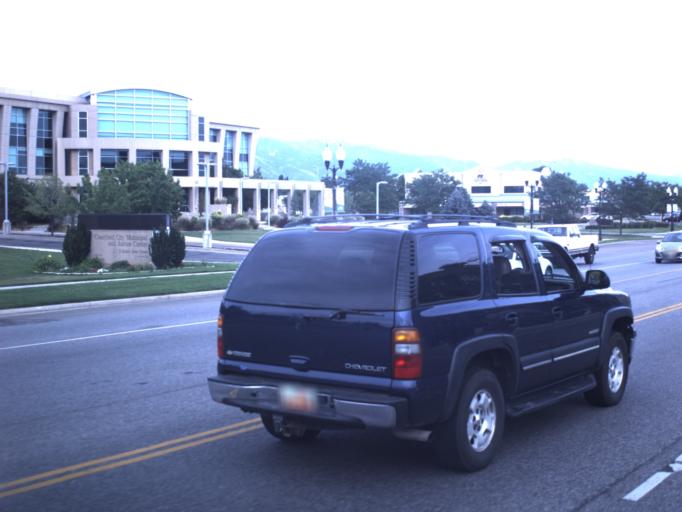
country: US
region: Utah
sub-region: Davis County
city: Clearfield
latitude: 41.1133
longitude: -112.0256
